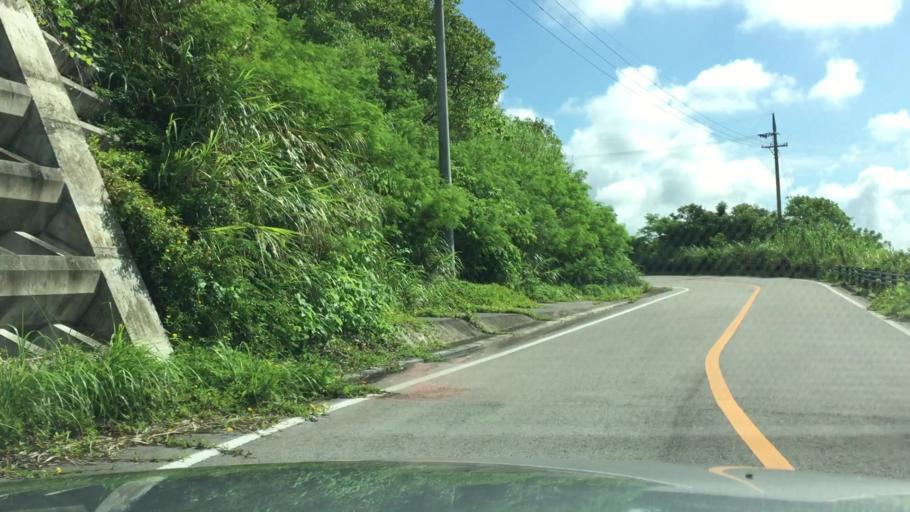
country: JP
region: Okinawa
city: Ishigaki
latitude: 24.3789
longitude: 124.1647
